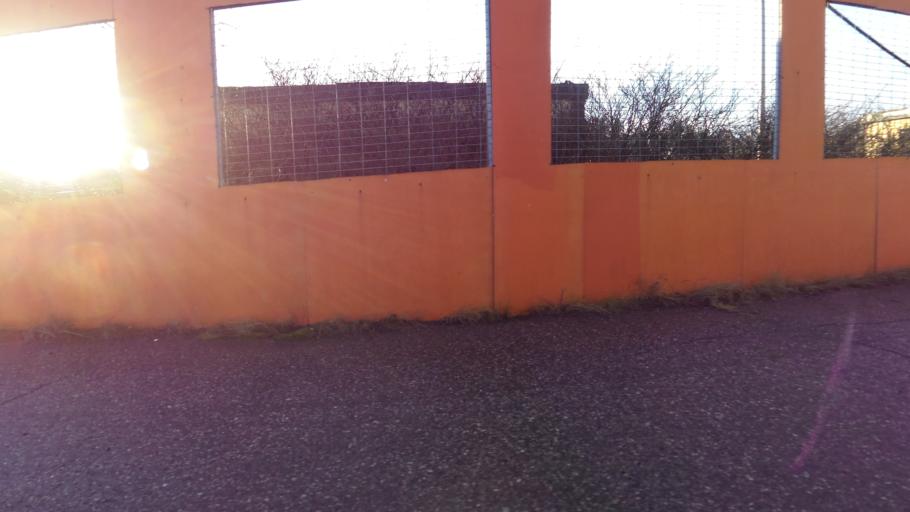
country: FI
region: Uusimaa
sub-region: Helsinki
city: Otaniemi
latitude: 60.1686
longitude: 24.8339
